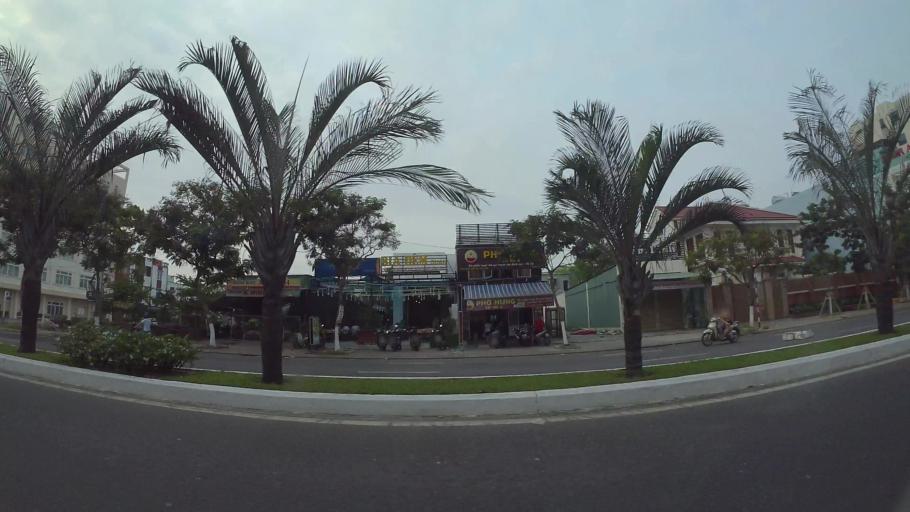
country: VN
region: Da Nang
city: Cam Le
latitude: 16.0315
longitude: 108.2133
